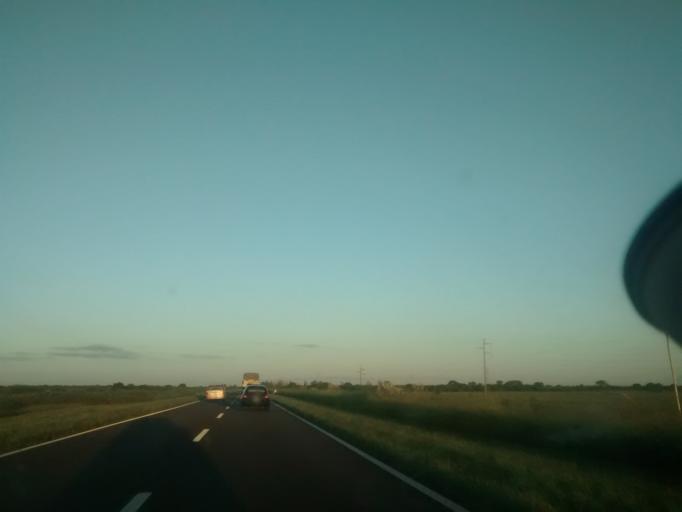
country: AR
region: Chaco
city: La Escondida
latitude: -27.1270
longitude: -59.5109
